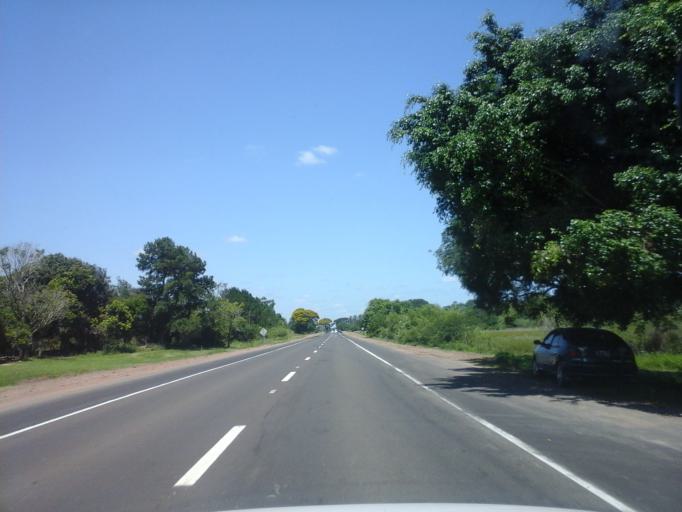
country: AR
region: Corrientes
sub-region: Departamento de Itati
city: Itati
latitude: -27.3660
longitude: -58.3065
